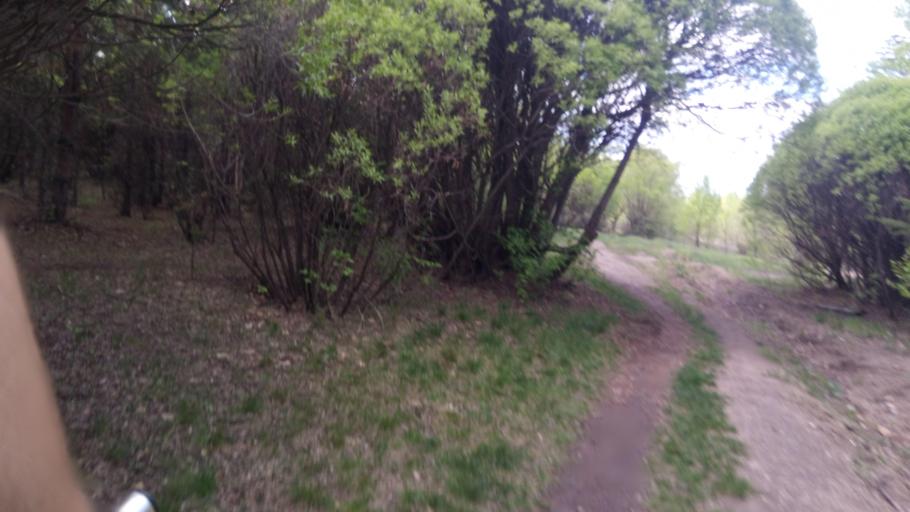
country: RU
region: Chelyabinsk
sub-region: Gorod Chelyabinsk
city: Chelyabinsk
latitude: 55.1689
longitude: 61.3410
